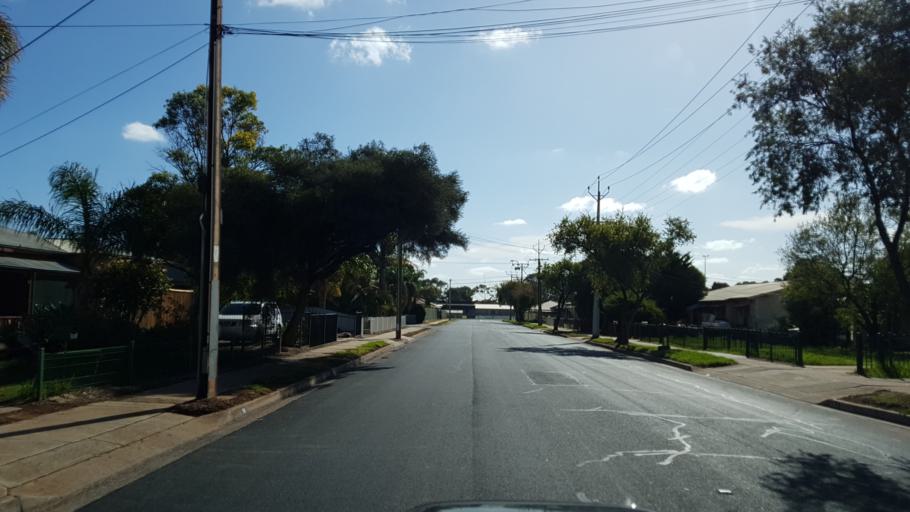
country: AU
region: South Australia
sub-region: Salisbury
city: Salisbury
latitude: -34.7497
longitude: 138.6305
